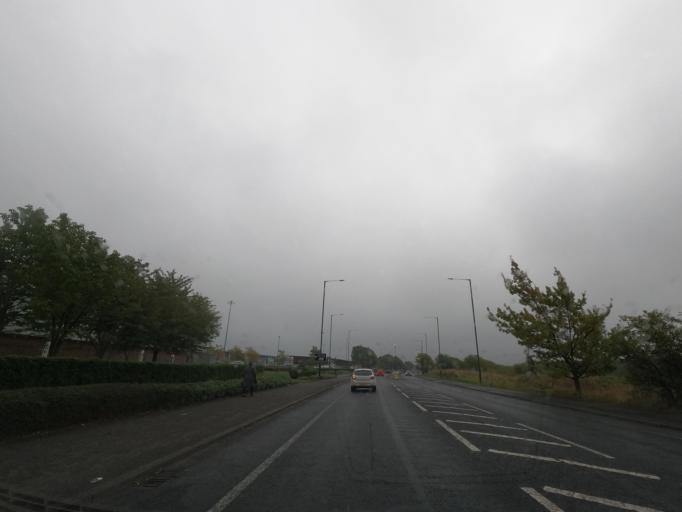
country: GB
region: England
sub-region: Redcar and Cleveland
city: South Bank
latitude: 54.5703
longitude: -1.1841
